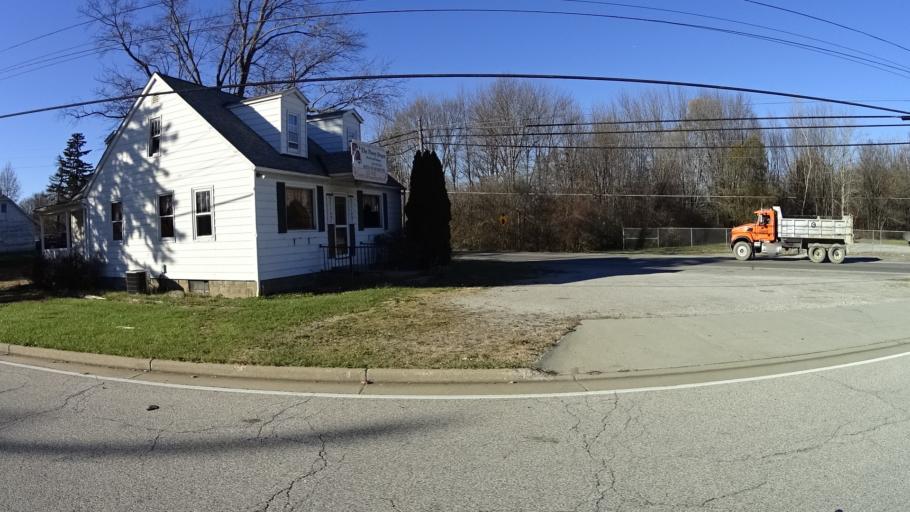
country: US
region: Ohio
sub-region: Lorain County
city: Elyria
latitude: 41.3363
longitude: -82.1225
